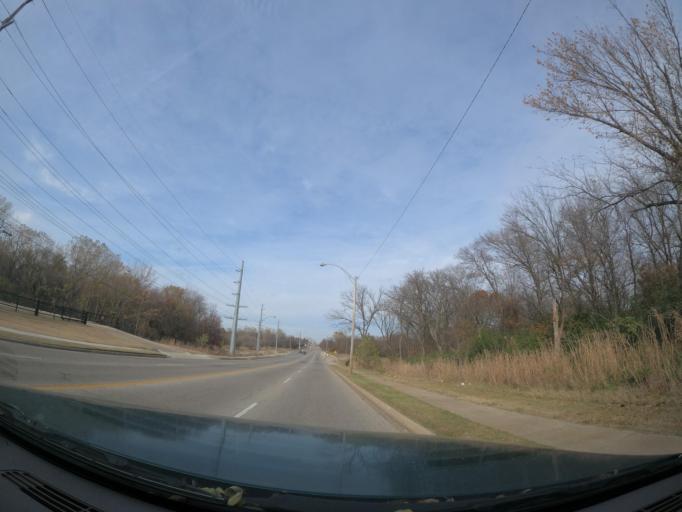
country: US
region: Oklahoma
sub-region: Tulsa County
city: Turley
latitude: 36.2115
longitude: -95.9755
